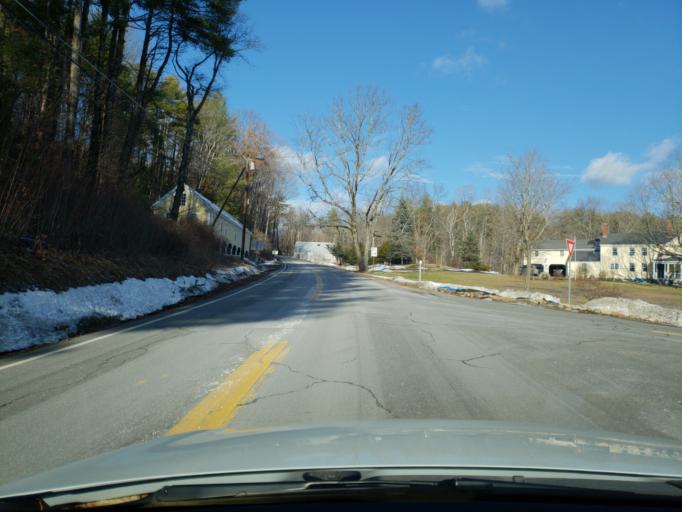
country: US
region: New Hampshire
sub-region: Hillsborough County
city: New Boston
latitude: 42.9812
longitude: -71.6931
